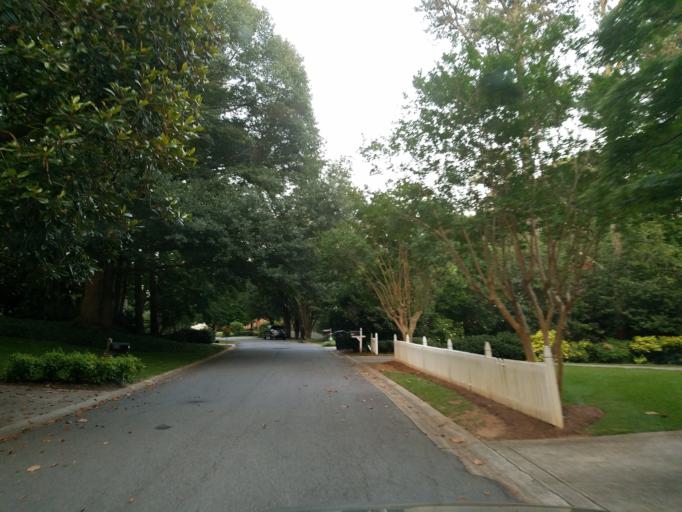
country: US
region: Georgia
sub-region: Cobb County
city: Vinings
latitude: 33.8601
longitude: -84.4613
